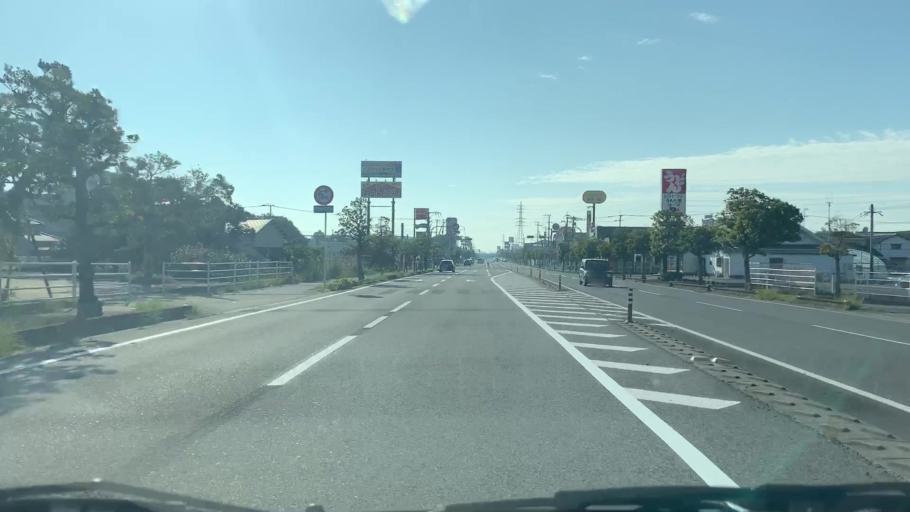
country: JP
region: Saga Prefecture
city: Saga-shi
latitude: 33.3062
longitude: 130.2779
